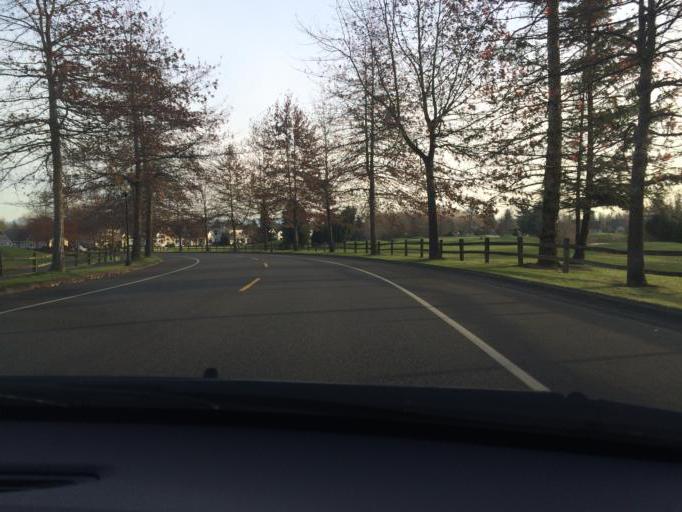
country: US
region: Washington
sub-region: Whatcom County
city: Lynden
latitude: 48.9588
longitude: -122.4446
